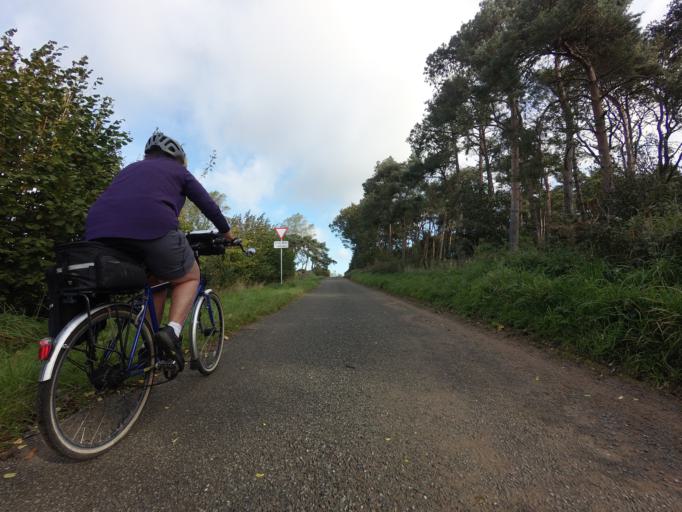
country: GB
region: England
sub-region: Norfolk
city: Dersingham
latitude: 52.8738
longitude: 0.6751
